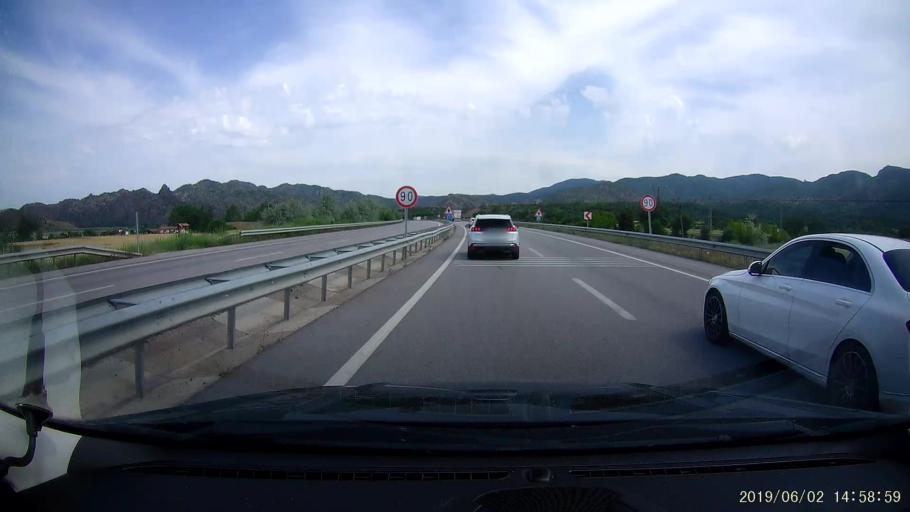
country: TR
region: Corum
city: Osmancik
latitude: 40.9740
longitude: 34.6882
